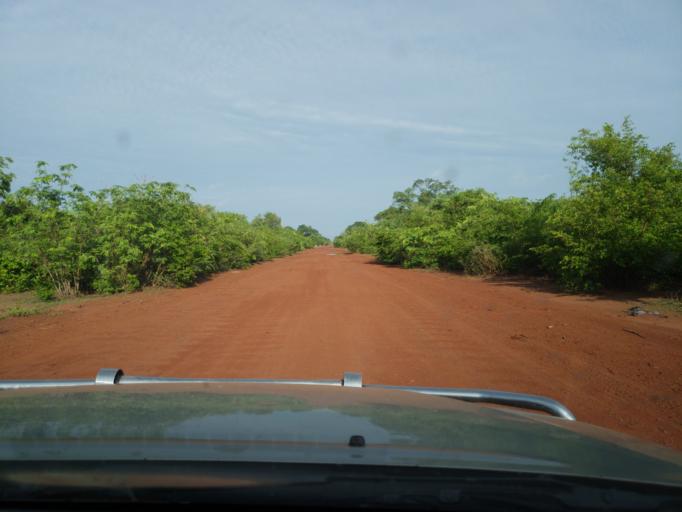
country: ML
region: Sikasso
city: Koutiala
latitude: 12.4171
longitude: -5.7137
